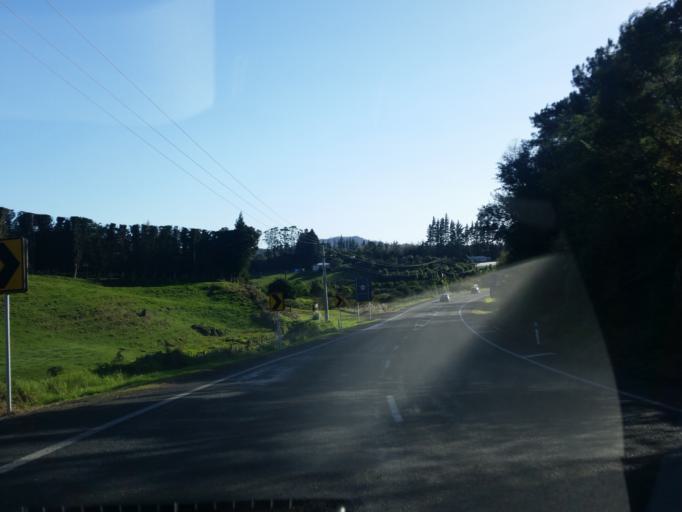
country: NZ
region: Bay of Plenty
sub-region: Western Bay of Plenty District
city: Katikati
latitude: -37.5469
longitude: 175.9104
